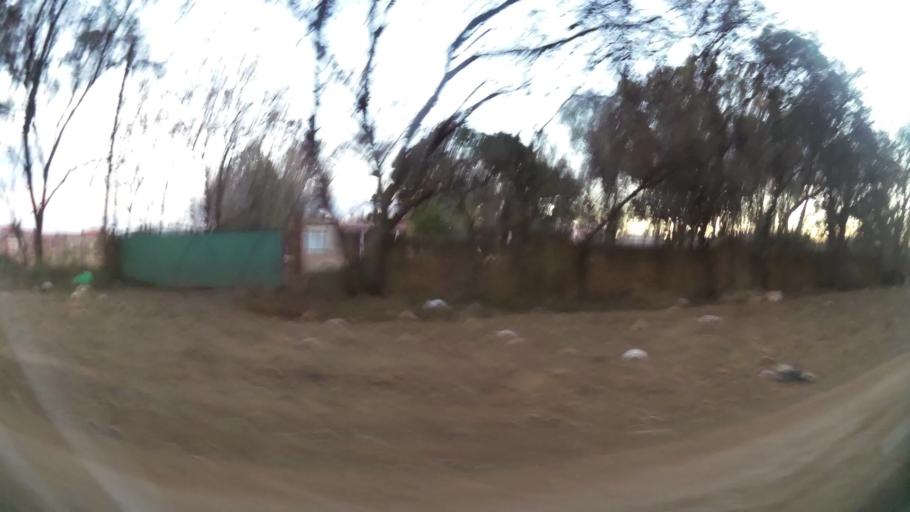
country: ZA
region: North-West
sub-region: Dr Kenneth Kaunda District Municipality
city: Potchefstroom
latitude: -26.7101
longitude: 27.1247
